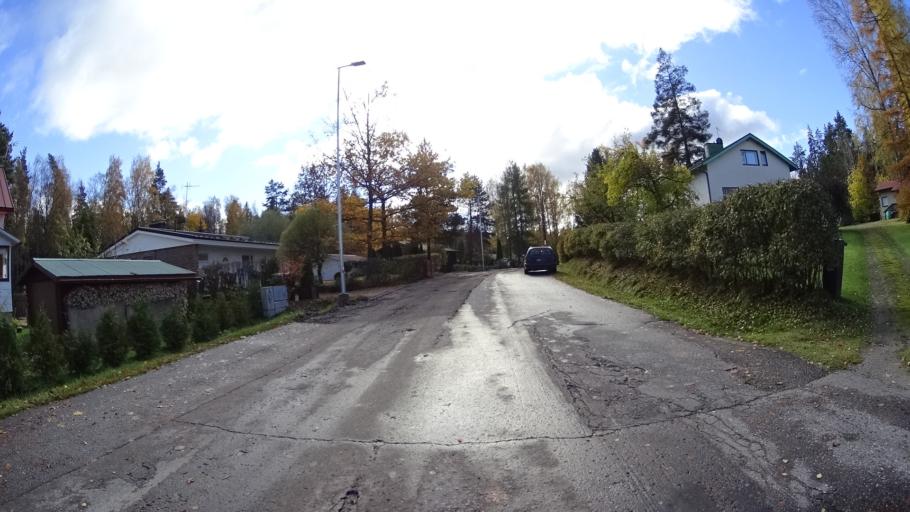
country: FI
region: Uusimaa
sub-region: Helsinki
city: Kilo
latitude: 60.2526
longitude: 24.8192
